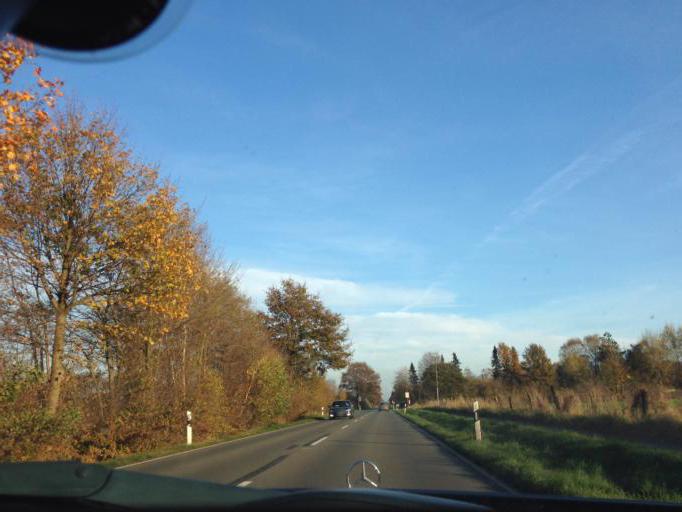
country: DE
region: Schleswig-Holstein
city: Stapelfeld
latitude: 53.6053
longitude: 10.1978
